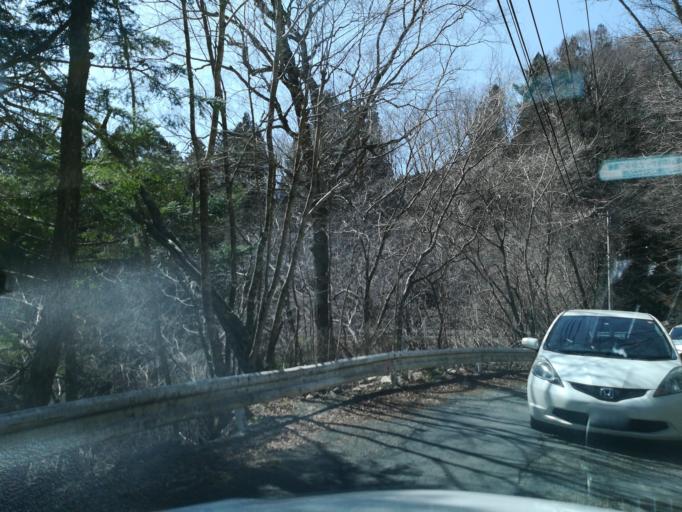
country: JP
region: Tokushima
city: Wakimachi
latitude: 33.8577
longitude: 134.0534
